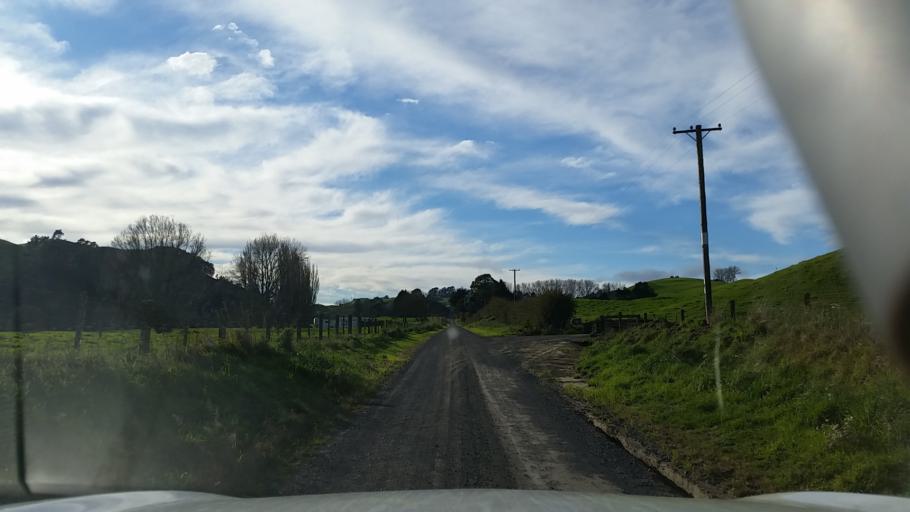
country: NZ
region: Waikato
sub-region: South Waikato District
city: Tokoroa
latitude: -38.3654
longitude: 176.0559
